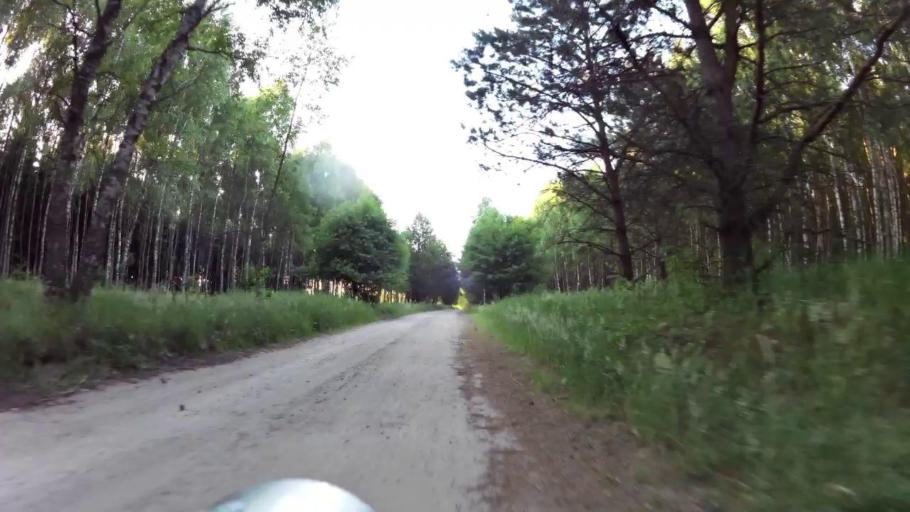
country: PL
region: West Pomeranian Voivodeship
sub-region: Powiat szczecinecki
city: Szczecinek
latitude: 53.8385
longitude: 16.6891
